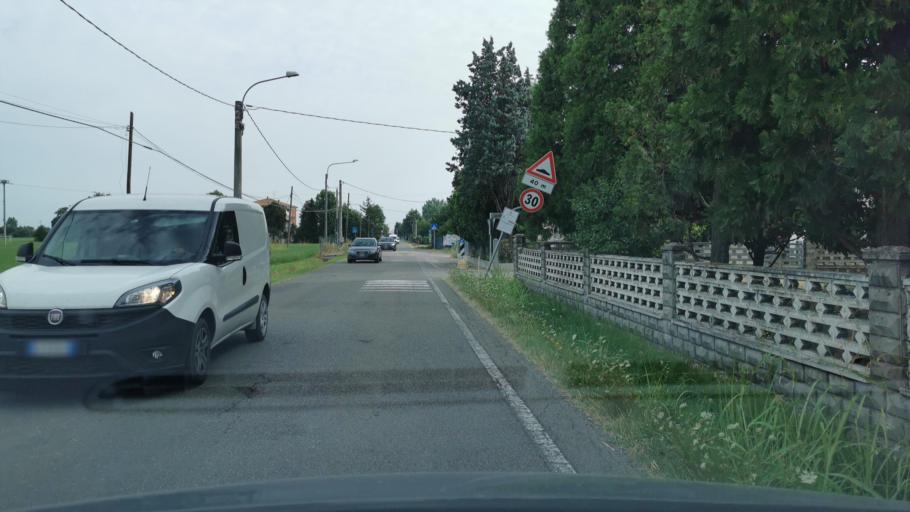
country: IT
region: Emilia-Romagna
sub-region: Provincia di Modena
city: Villanova
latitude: 44.6809
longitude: 10.9067
